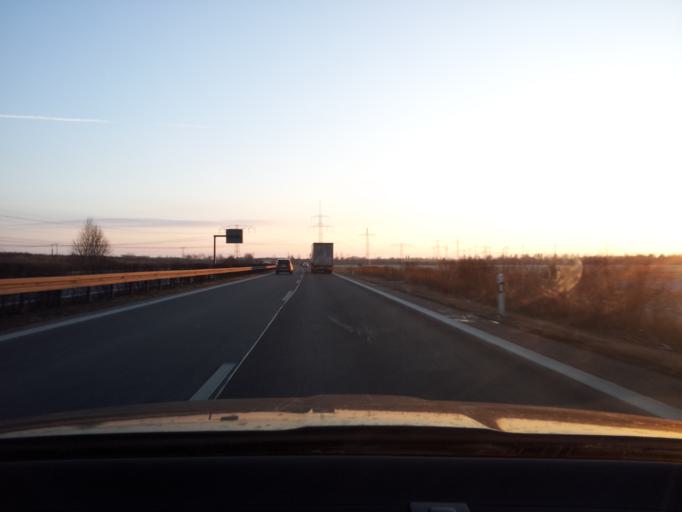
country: DE
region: Brandenburg
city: Brieselang
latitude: 52.6097
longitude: 12.9720
